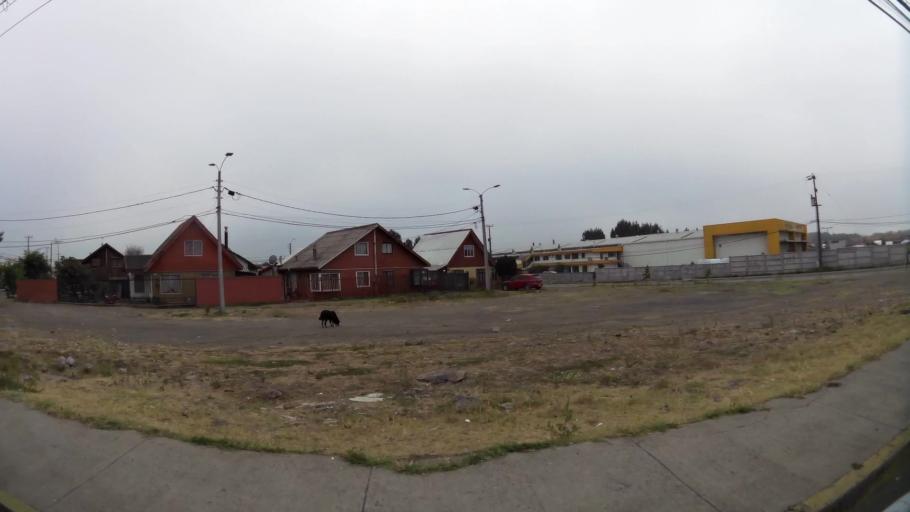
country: CL
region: Biobio
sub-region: Provincia de Concepcion
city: Concepcion
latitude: -36.7961
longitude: -73.0819
